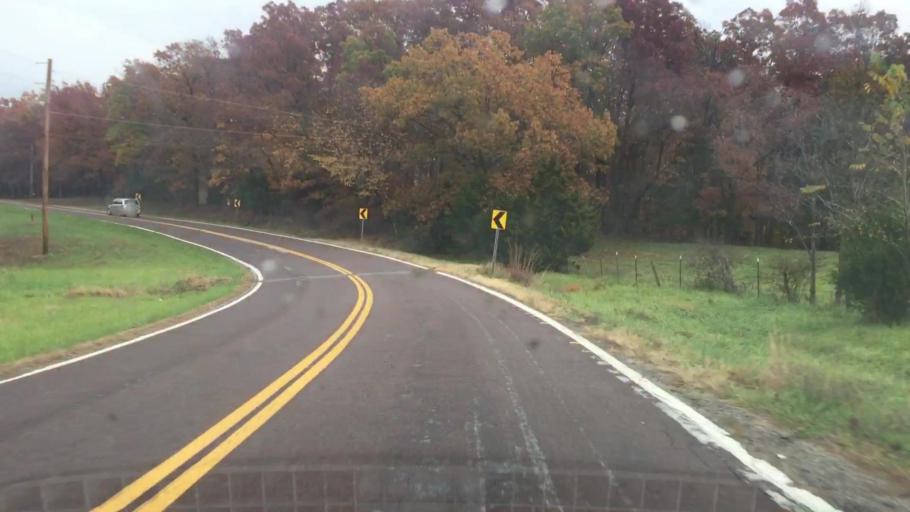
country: US
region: Missouri
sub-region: Callaway County
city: Fulton
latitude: 38.7800
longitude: -91.8305
